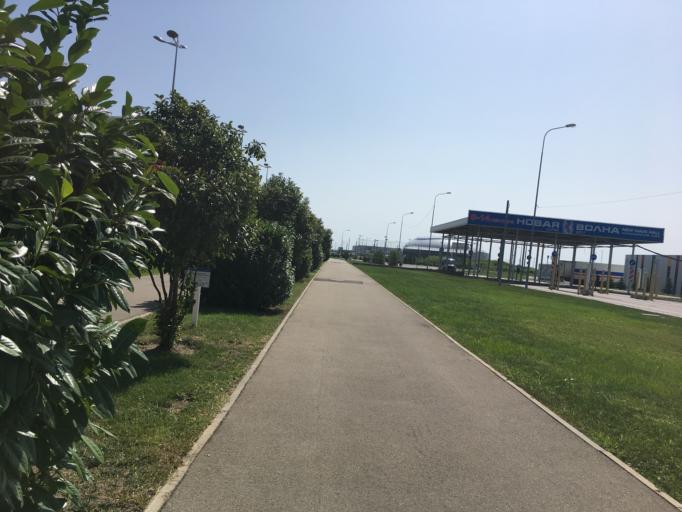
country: RU
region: Krasnodarskiy
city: Adler
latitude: 43.4134
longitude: 39.9486
